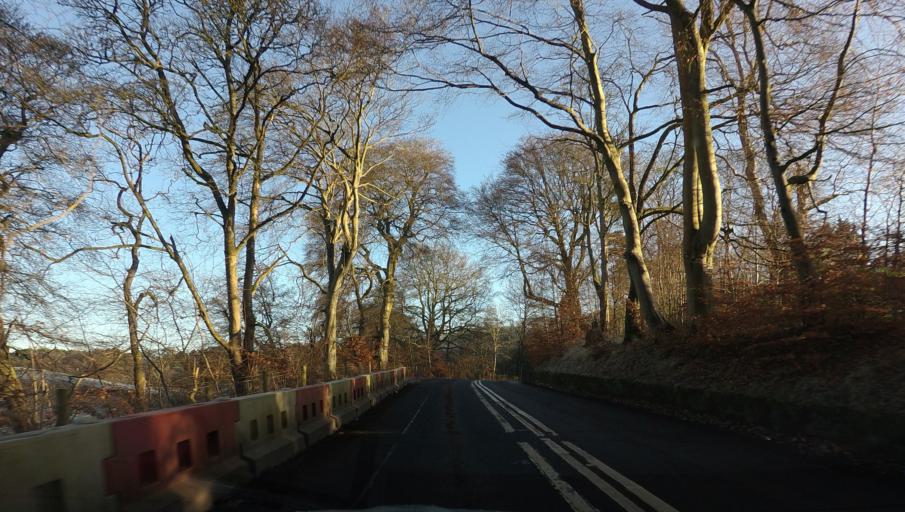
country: GB
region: Scotland
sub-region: North Lanarkshire
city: Newmains
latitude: 55.7954
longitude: -3.8545
